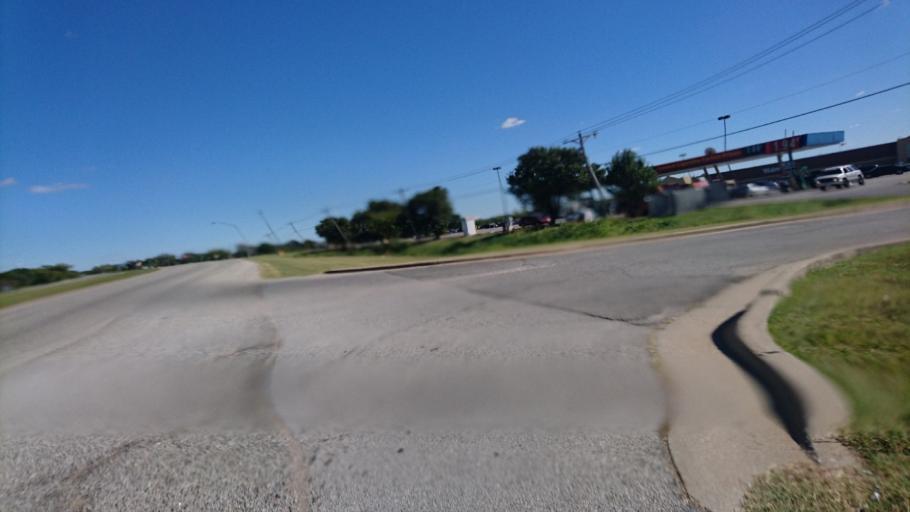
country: US
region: Oklahoma
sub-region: Creek County
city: Sapulpa
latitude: 35.9884
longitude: -96.1360
